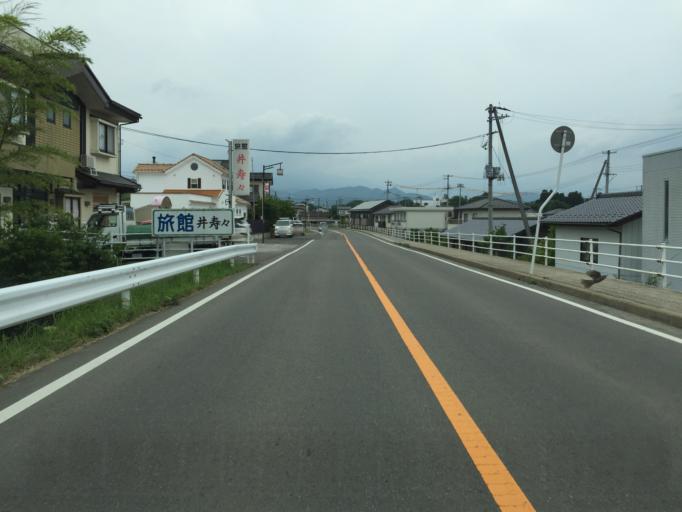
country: JP
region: Fukushima
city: Nihommatsu
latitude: 37.6550
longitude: 140.4828
